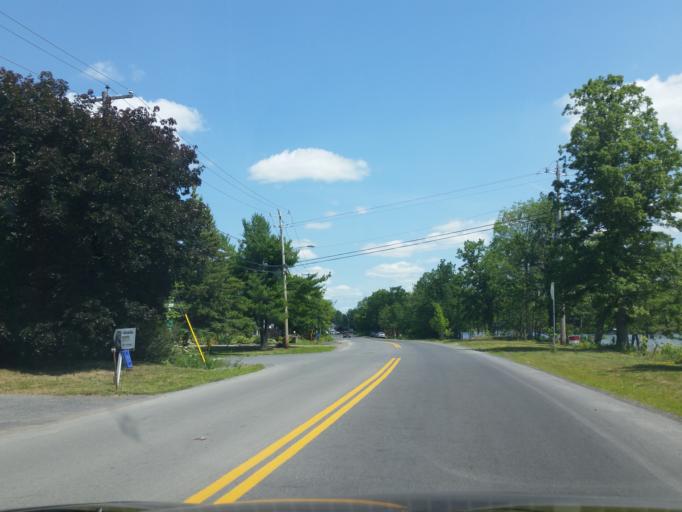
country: CA
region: Quebec
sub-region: Monteregie
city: Saint-Jean-sur-Richelieu
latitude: 45.3700
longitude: -73.2609
